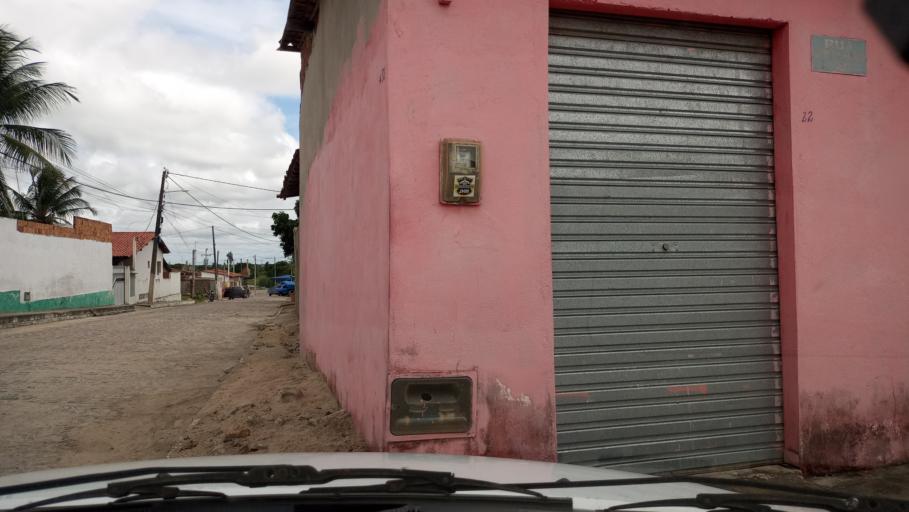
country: BR
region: Rio Grande do Norte
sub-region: Brejinho
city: Brejinho
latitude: -6.1532
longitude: -35.4369
